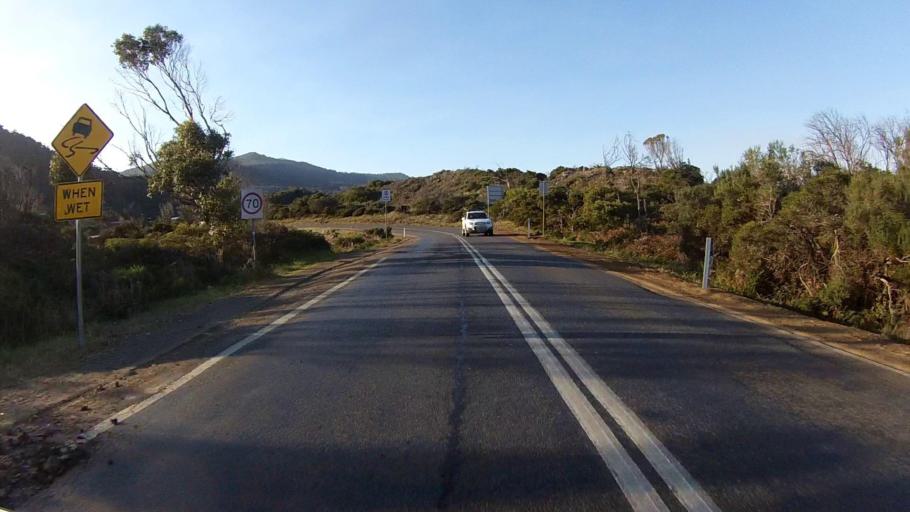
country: AU
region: Tasmania
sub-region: Sorell
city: Sorell
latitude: -43.0178
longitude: 147.9240
